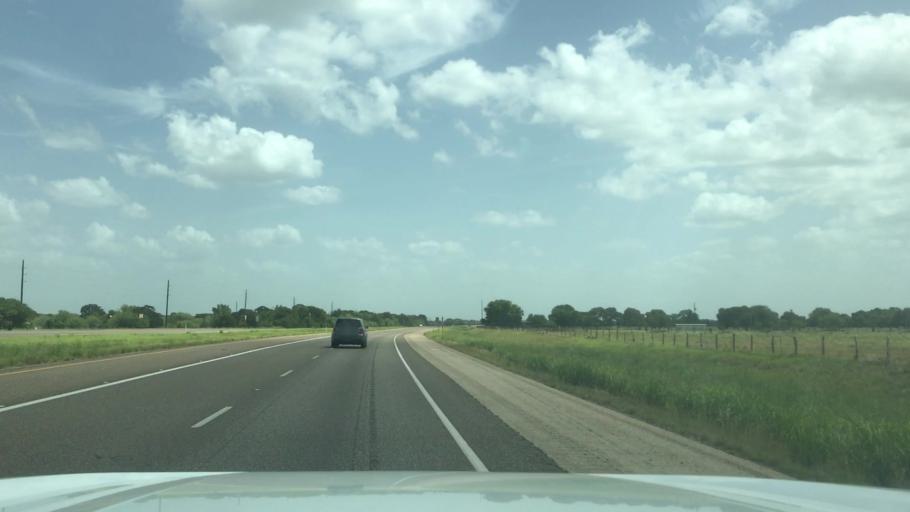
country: US
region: Texas
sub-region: Robertson County
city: Calvert
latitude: 31.0031
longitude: -96.6968
